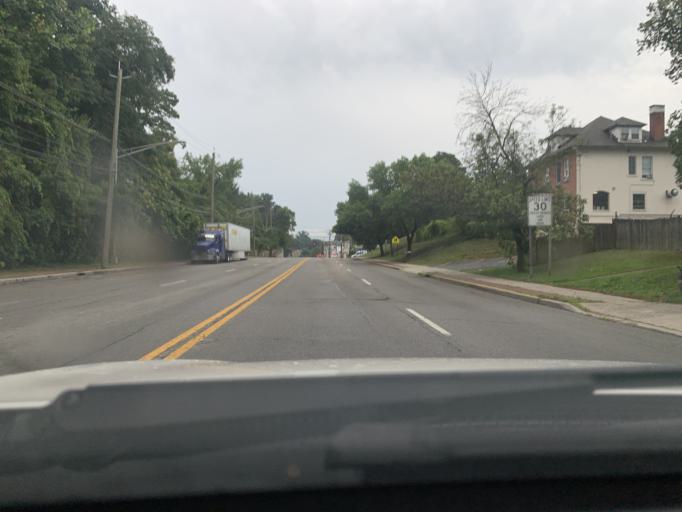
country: US
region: New York
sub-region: Westchester County
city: Ossining
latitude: 41.1692
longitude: -73.8638
